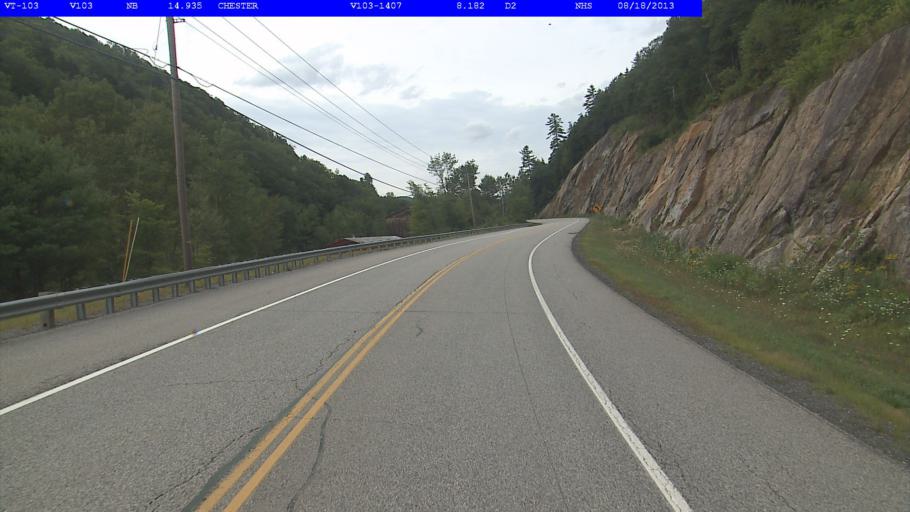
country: US
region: Vermont
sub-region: Windsor County
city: Chester
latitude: 43.3289
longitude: -72.6148
